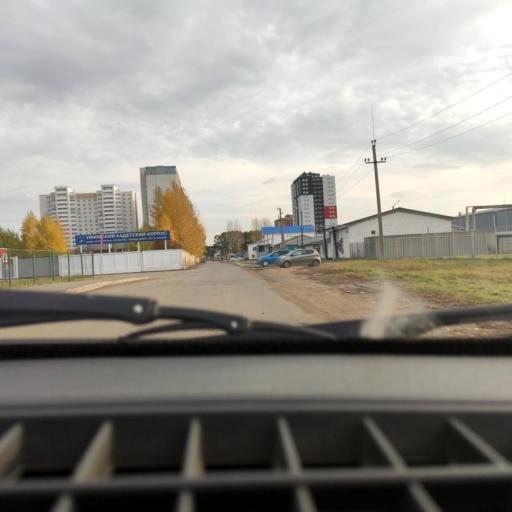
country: RU
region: Bashkortostan
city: Mikhaylovka
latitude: 54.7949
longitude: 55.8523
